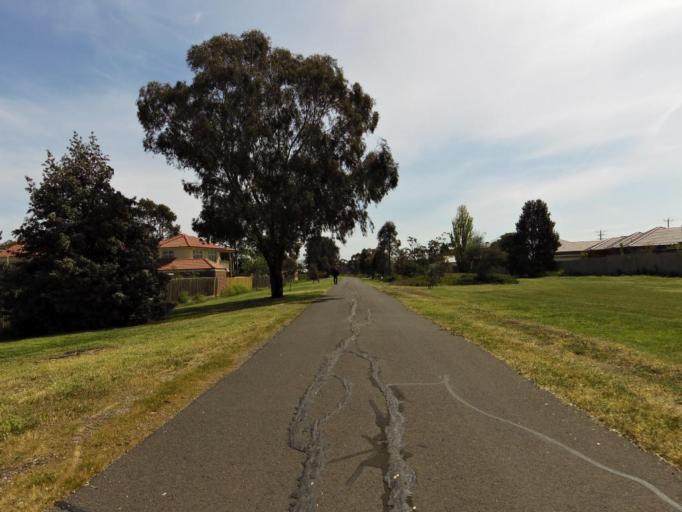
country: AU
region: Victoria
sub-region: Brimbank
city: Brooklyn
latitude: -37.8214
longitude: 144.8422
